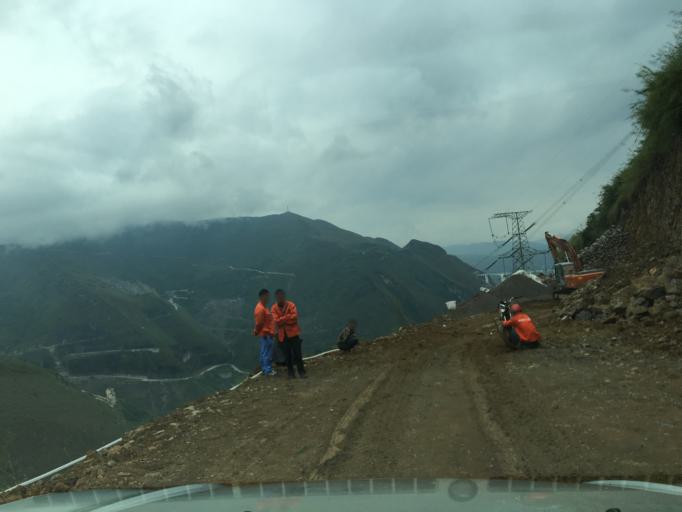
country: CN
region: Guizhou Sheng
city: Liupanshui
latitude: 25.9621
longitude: 105.2382
